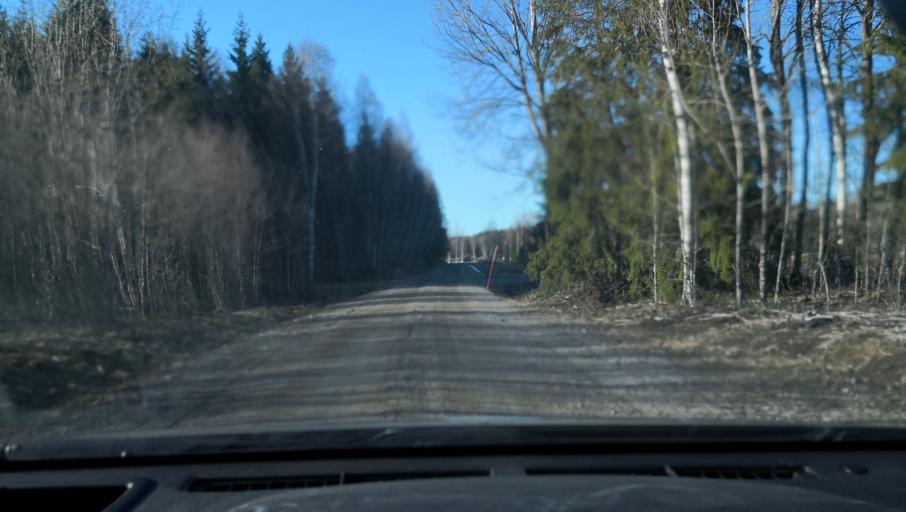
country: SE
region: Dalarna
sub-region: Avesta Kommun
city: Horndal
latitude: 60.1790
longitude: 16.6285
